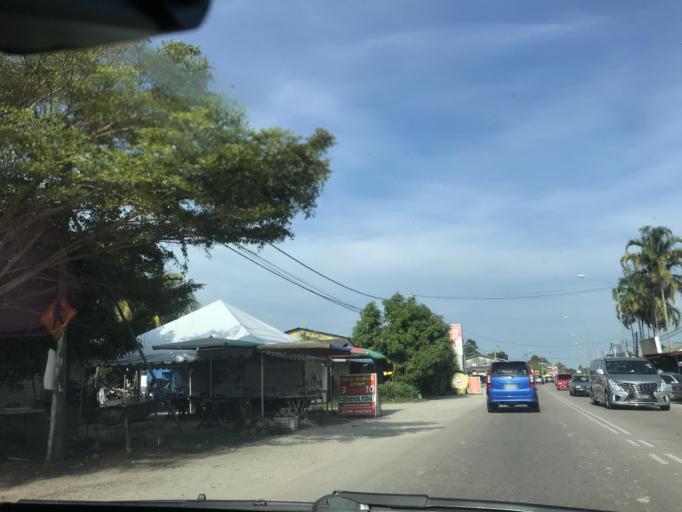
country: MY
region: Kelantan
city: Kota Bharu
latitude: 6.1238
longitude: 102.2788
